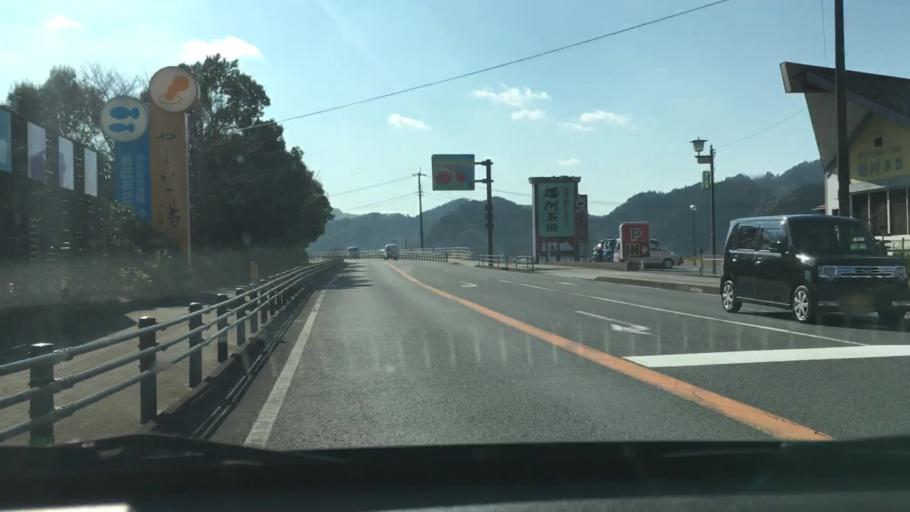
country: JP
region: Oita
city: Saiki
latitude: 32.9645
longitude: 131.8381
